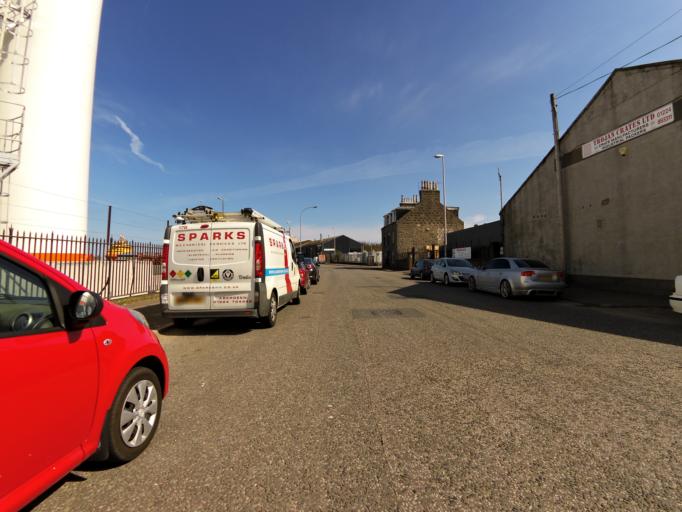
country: GB
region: Scotland
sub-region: Aberdeen City
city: Aberdeen
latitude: 57.1383
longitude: -2.0813
